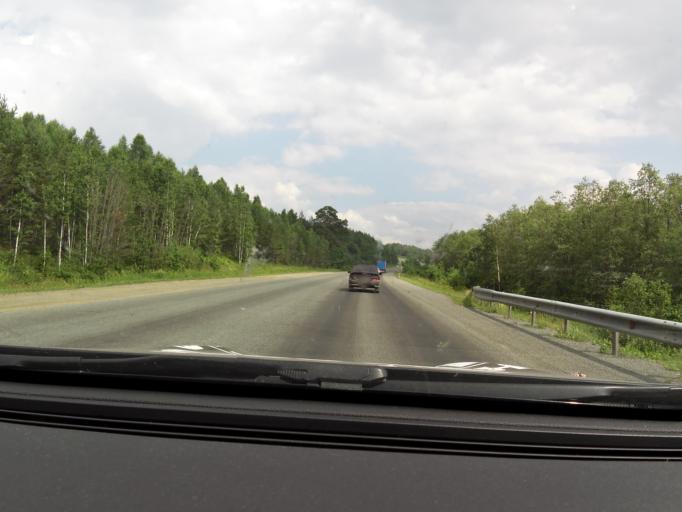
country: RU
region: Sverdlovsk
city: Ufimskiy
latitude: 56.7755
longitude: 58.2303
